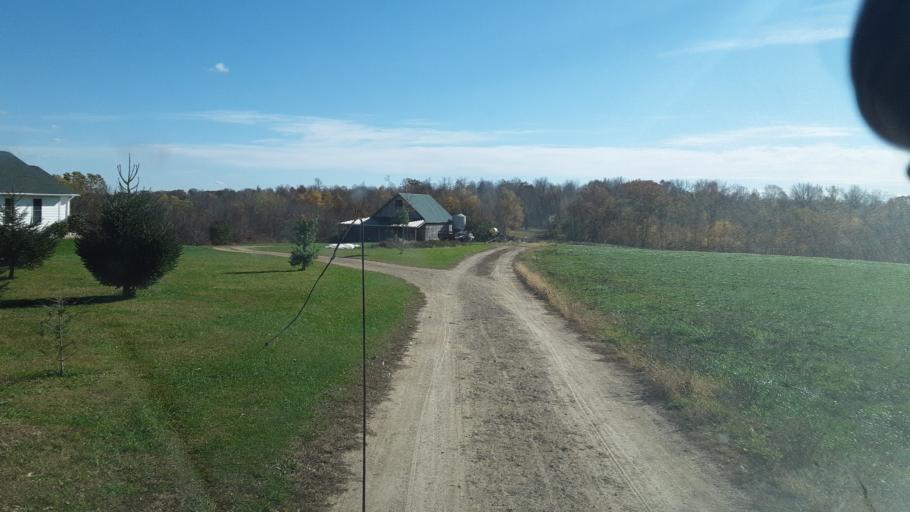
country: US
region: Wisconsin
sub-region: Vernon County
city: Hillsboro
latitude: 43.6834
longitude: -90.4090
